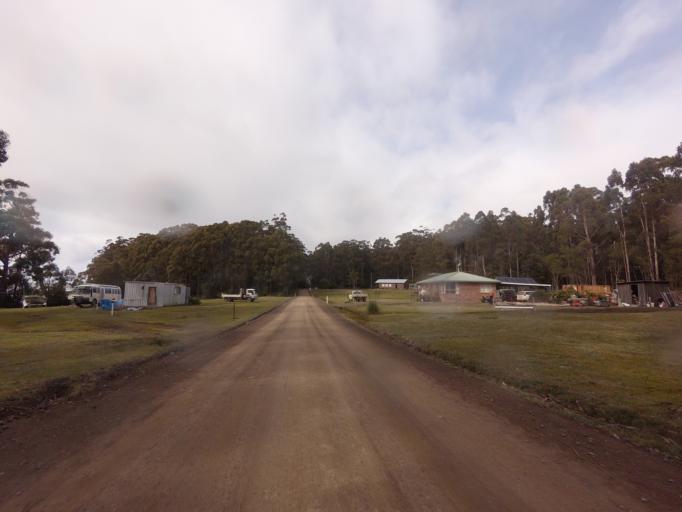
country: AU
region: Tasmania
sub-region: Huon Valley
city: Geeveston
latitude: -43.5383
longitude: 146.8916
